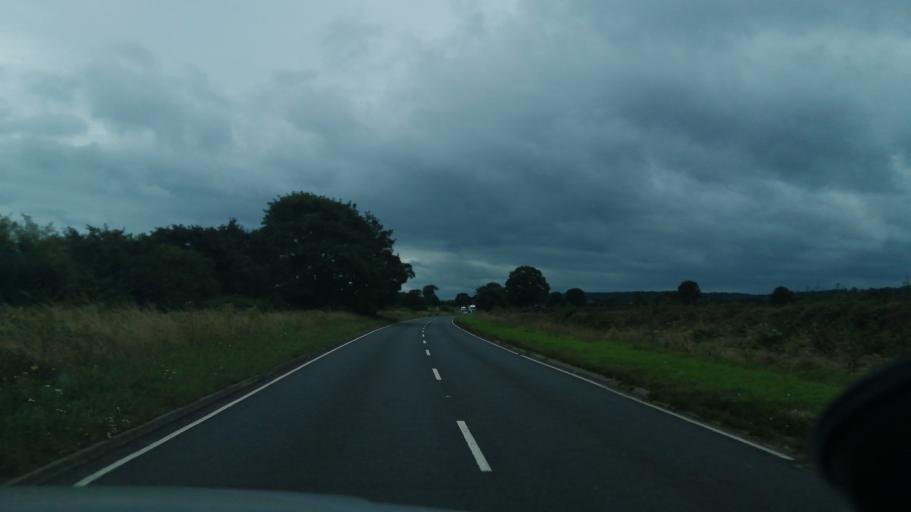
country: GB
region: England
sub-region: Herefordshire
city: Thruxton
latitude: 52.0114
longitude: -2.7885
